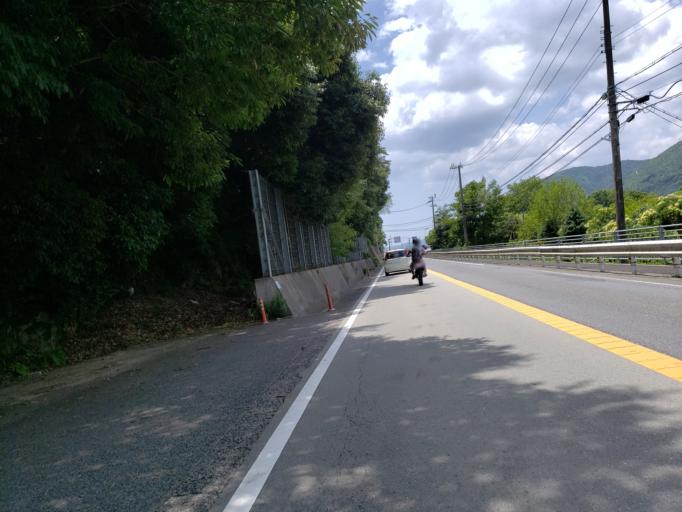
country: JP
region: Hyogo
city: Aioi
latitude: 34.7738
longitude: 134.4309
